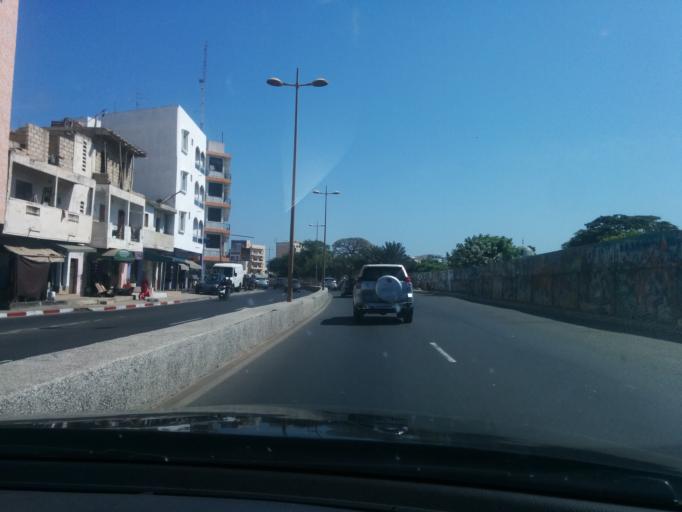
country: SN
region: Dakar
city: Dakar
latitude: 14.6766
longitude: -17.4565
